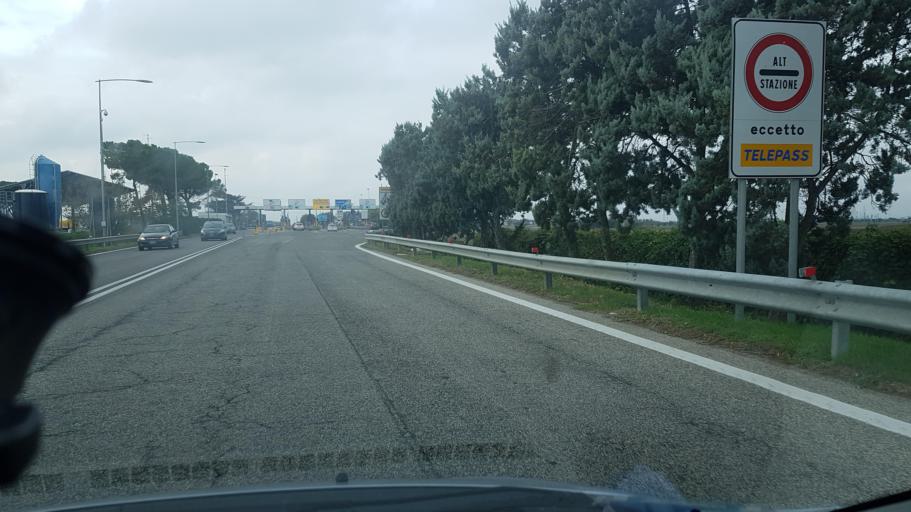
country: IT
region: Apulia
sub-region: Provincia di Foggia
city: Foggia
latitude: 41.4992
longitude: 15.5673
